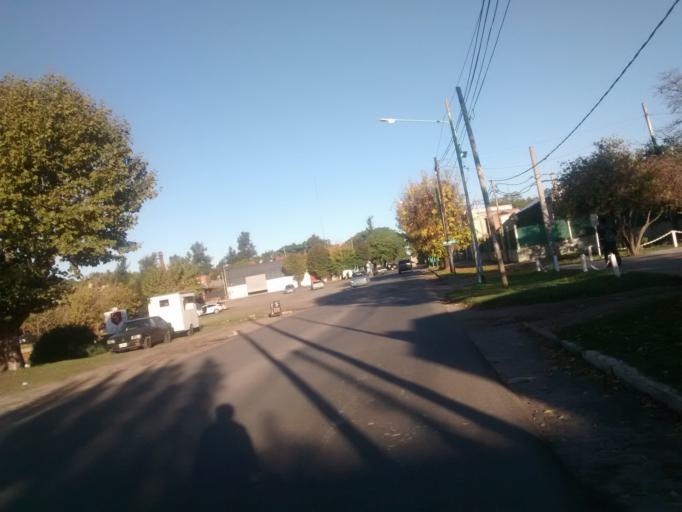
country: AR
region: Buenos Aires
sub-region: Partido de La Plata
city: La Plata
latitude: -34.8975
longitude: -57.9329
